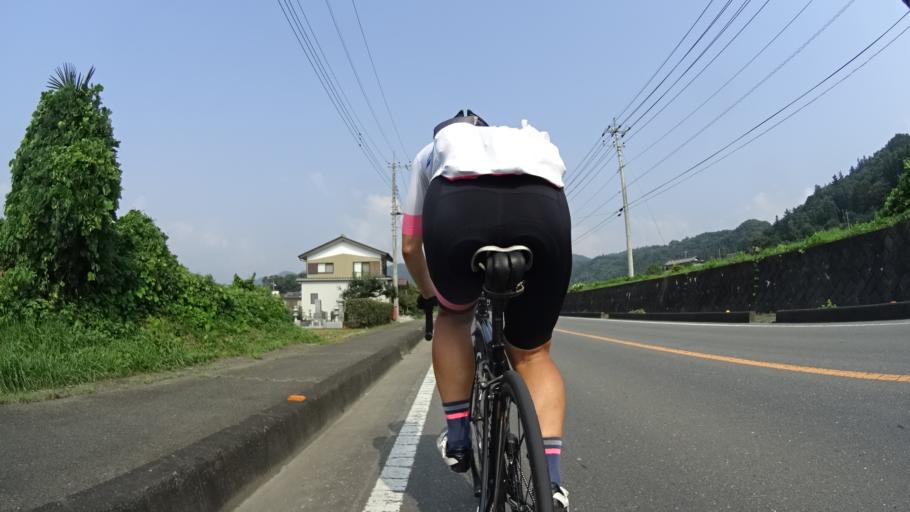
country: JP
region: Saitama
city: Chichibu
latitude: 36.0278
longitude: 138.9928
